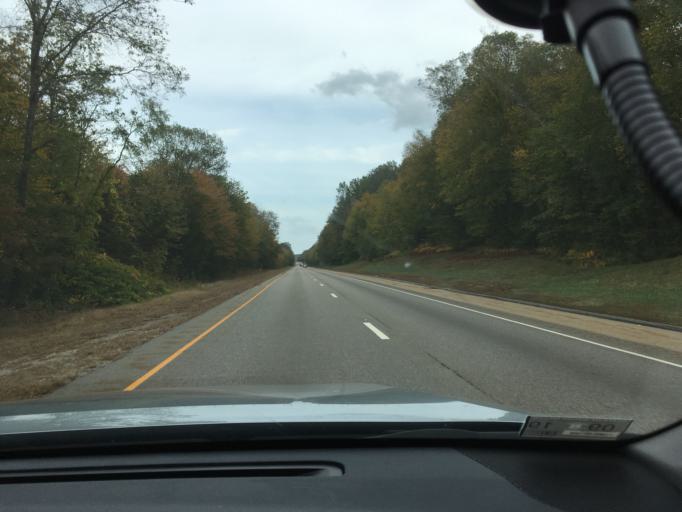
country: US
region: Connecticut
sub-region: New London County
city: Colchester
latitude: 41.5692
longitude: -72.2805
